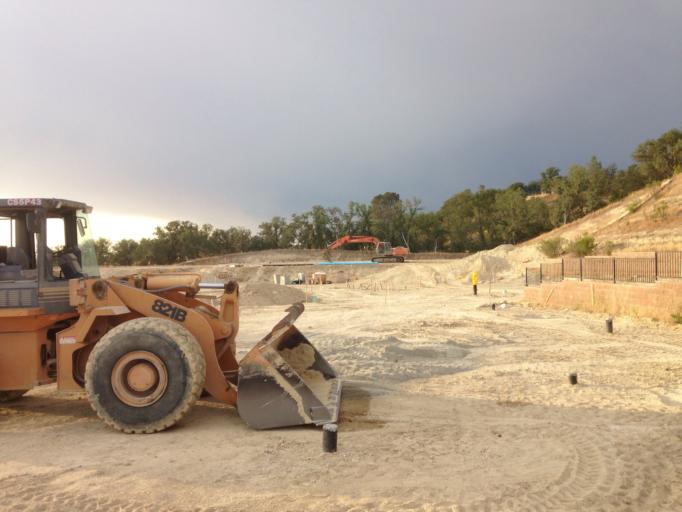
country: US
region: California
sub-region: San Luis Obispo County
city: Atascadero
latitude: 35.4559
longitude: -120.6284
